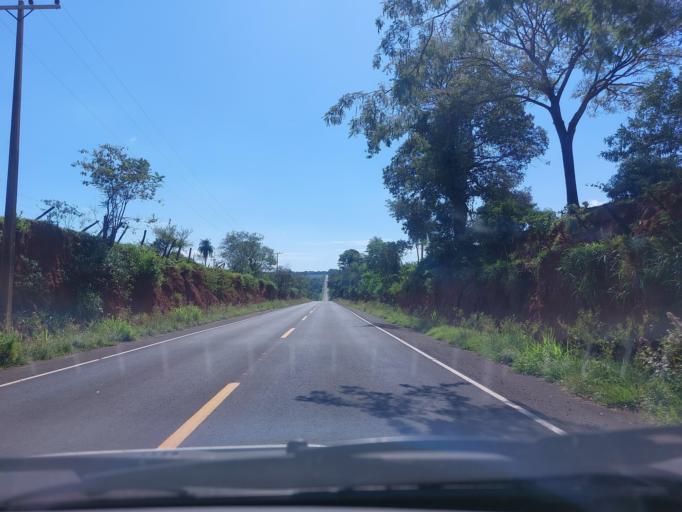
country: PY
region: San Pedro
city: Guayaybi
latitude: -24.5558
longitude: -56.5196
